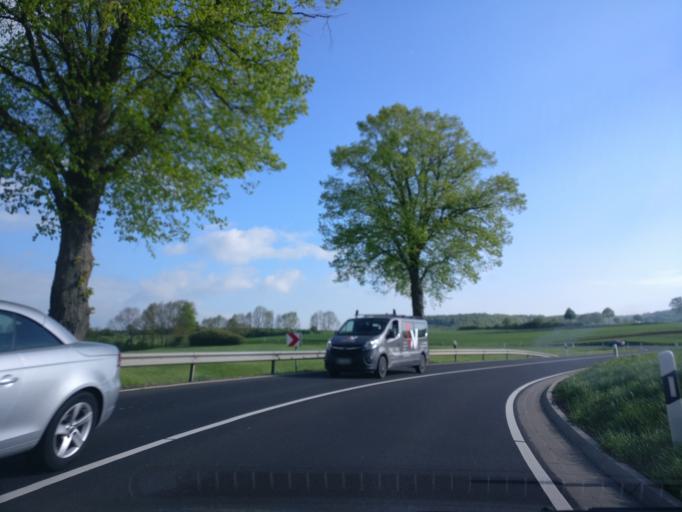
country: DE
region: Lower Saxony
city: Scheden
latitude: 51.4662
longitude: 9.7199
